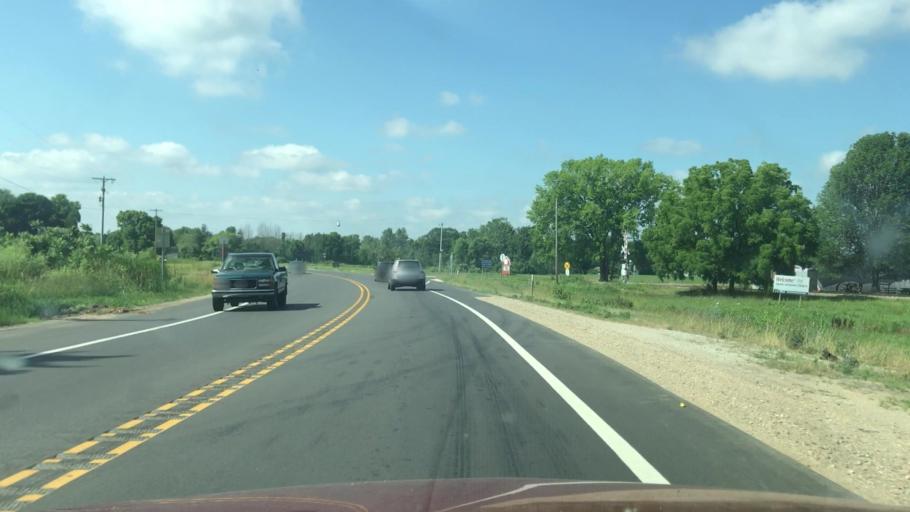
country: US
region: Michigan
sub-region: Newaygo County
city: Newaygo
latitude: 43.3520
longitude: -85.8107
